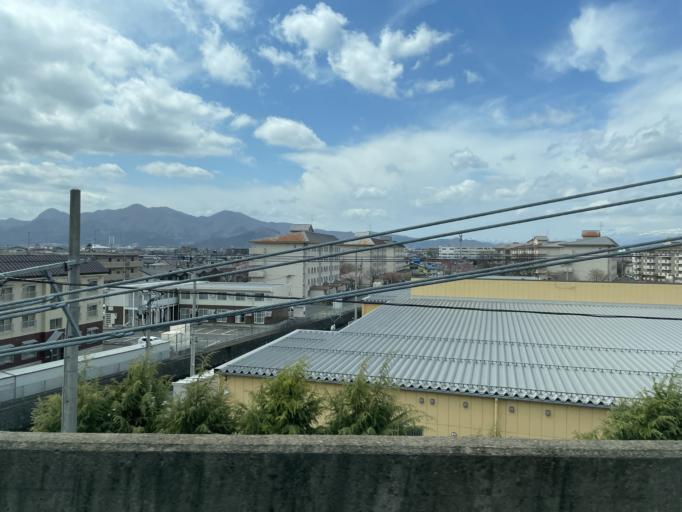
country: JP
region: Iwate
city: Morioka-shi
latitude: 39.6855
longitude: 141.1479
